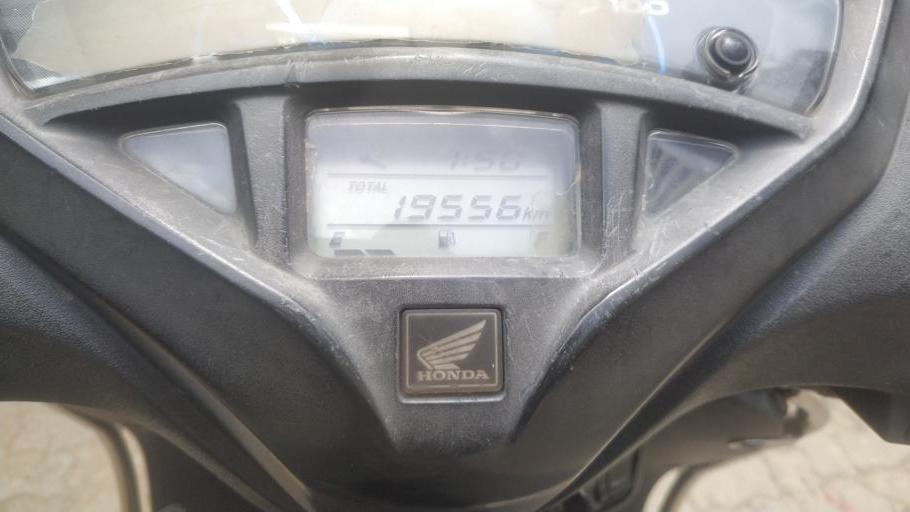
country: IN
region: Maharashtra
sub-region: Mumbai Suburban
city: Mumbai
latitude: 19.0019
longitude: 72.8251
